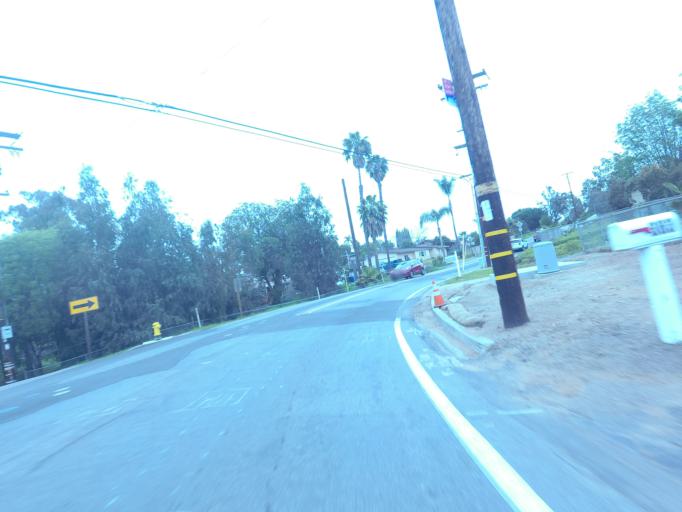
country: US
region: California
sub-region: San Diego County
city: Vista
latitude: 33.2378
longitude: -117.2450
